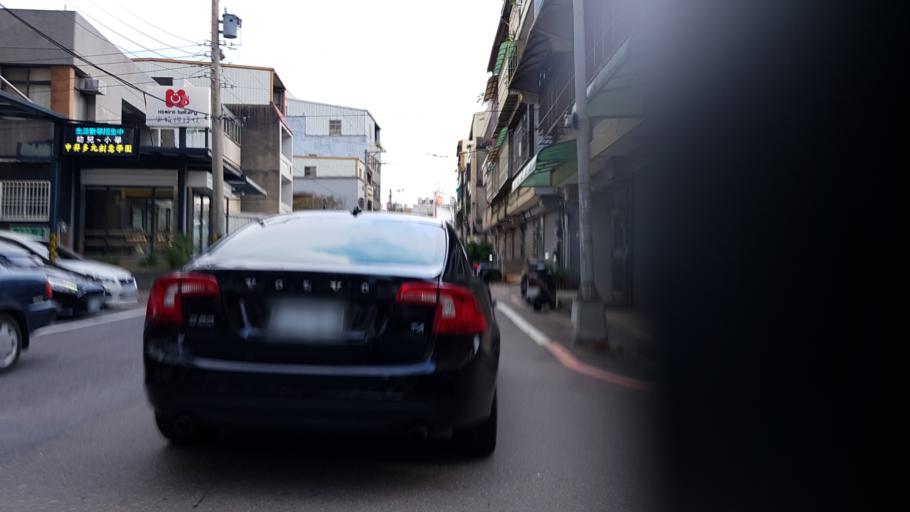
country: TW
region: Taiwan
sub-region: Hsinchu
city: Hsinchu
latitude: 24.7879
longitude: 121.0112
